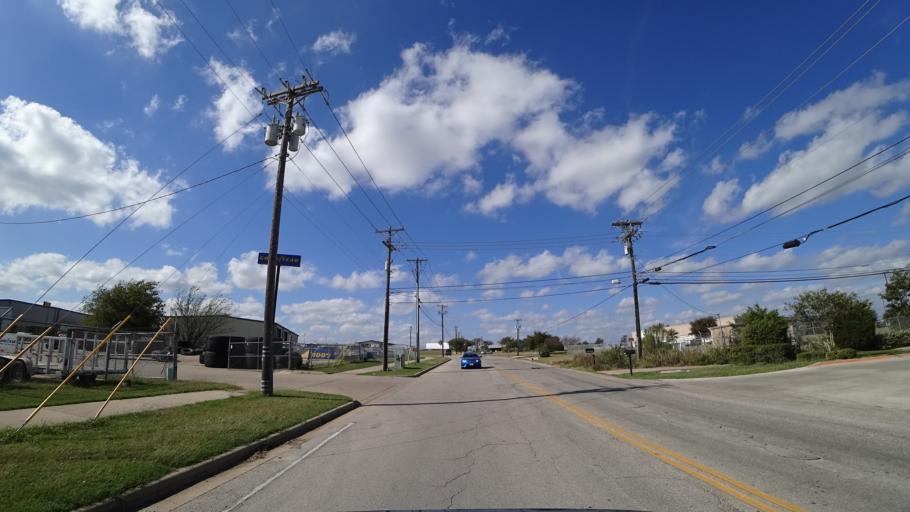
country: US
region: Texas
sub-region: Travis County
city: Windemere
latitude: 30.4613
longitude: -97.6583
